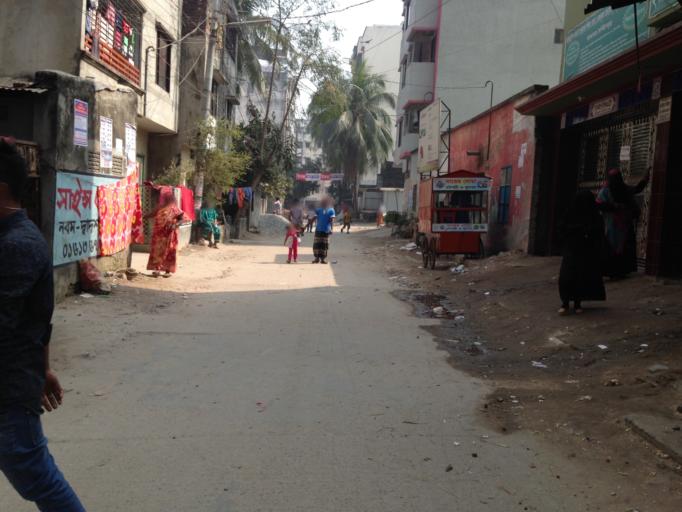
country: BD
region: Dhaka
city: Azimpur
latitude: 23.8083
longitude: 90.3772
